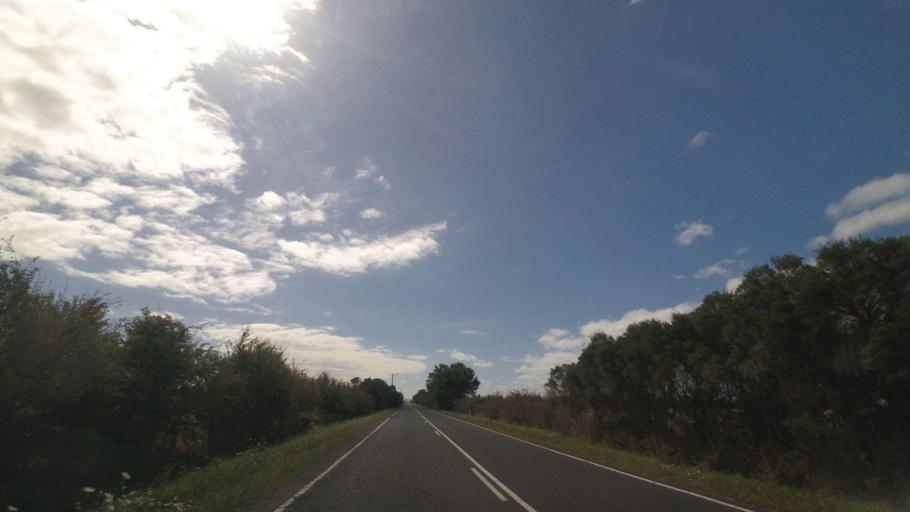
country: AU
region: Victoria
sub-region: Cardinia
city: Garfield
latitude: -38.2112
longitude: 145.6361
